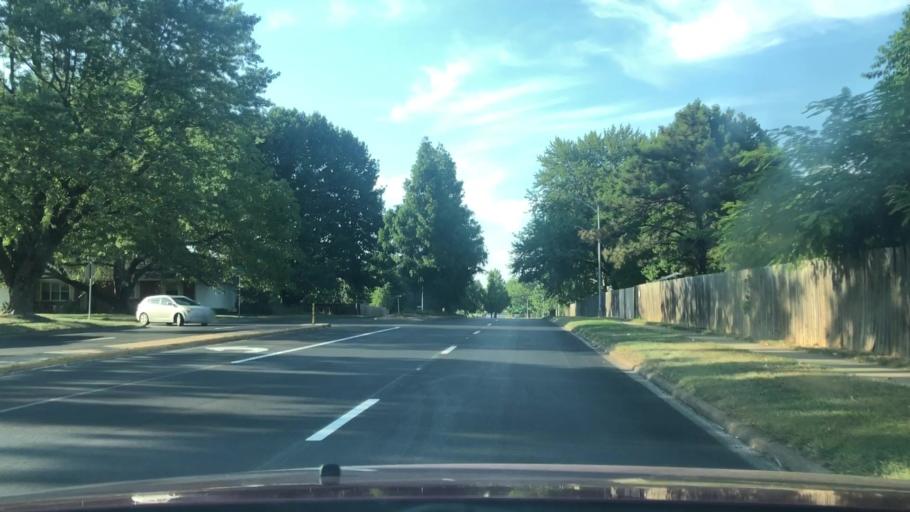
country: US
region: Missouri
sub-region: Greene County
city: Springfield
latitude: 37.1645
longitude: -93.2770
